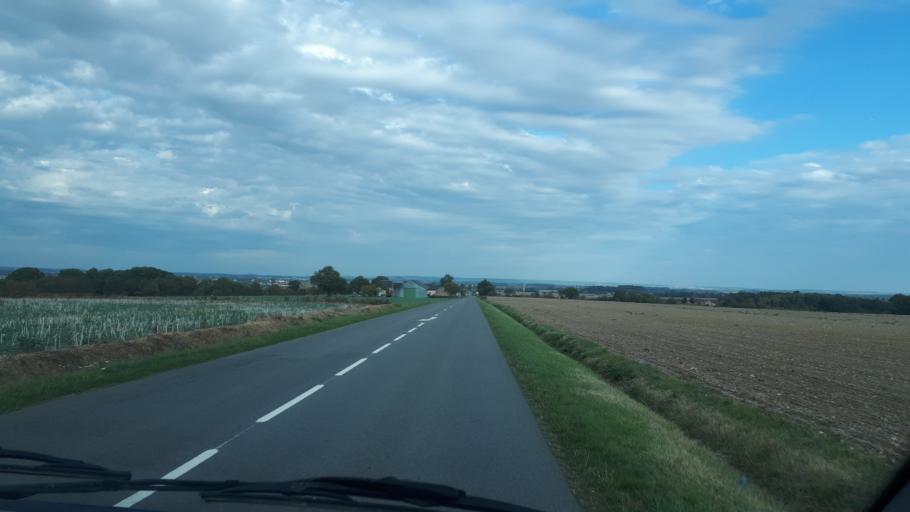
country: FR
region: Centre
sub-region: Departement du Loir-et-Cher
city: Mondoubleau
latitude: 47.9601
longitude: 0.9299
